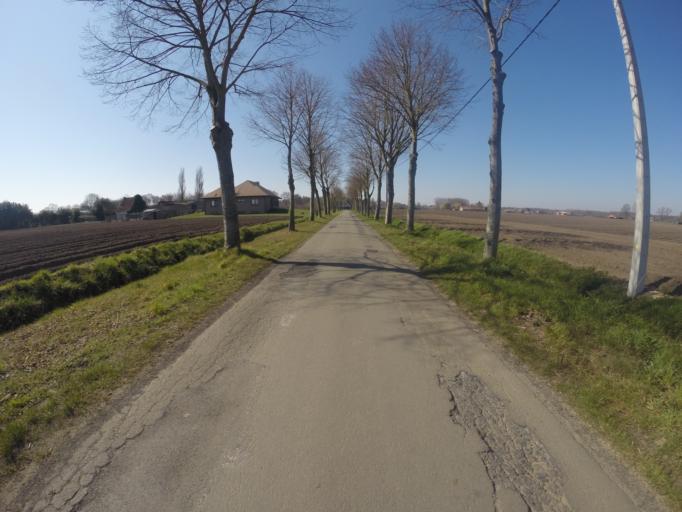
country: BE
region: Flanders
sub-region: Provincie Oost-Vlaanderen
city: Knesselare
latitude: 51.1118
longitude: 3.3963
